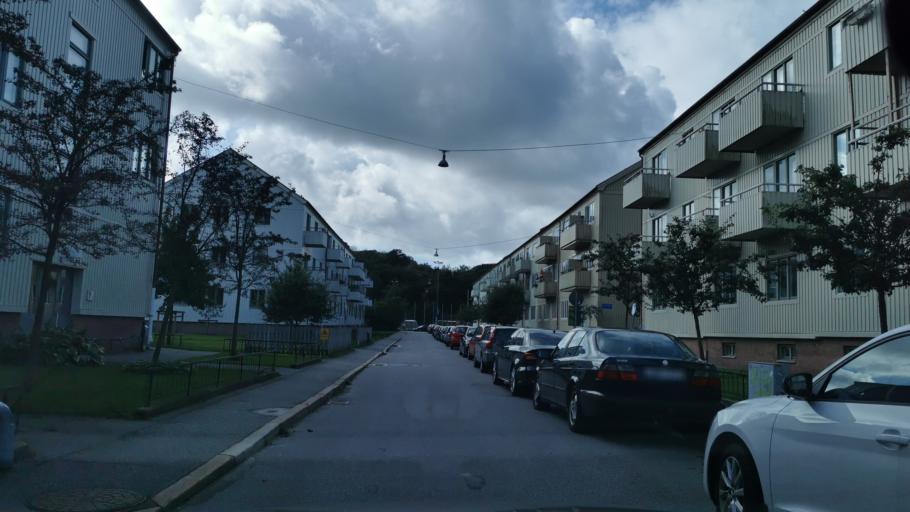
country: SE
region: Vaestra Goetaland
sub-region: Goteborg
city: Majorna
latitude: 57.6912
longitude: 11.9368
